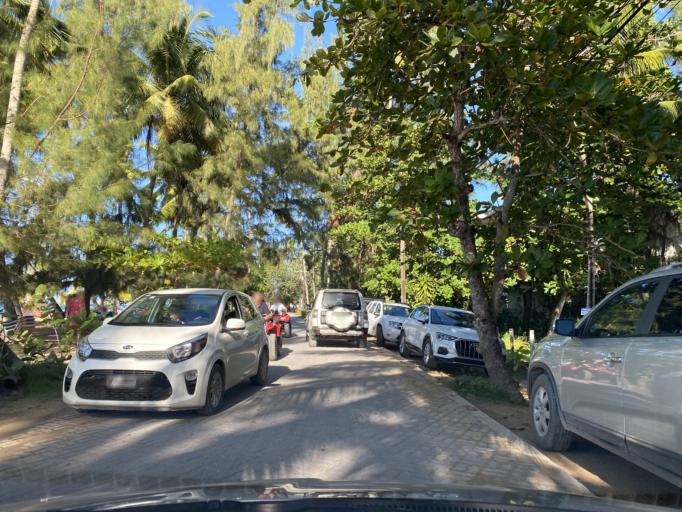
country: DO
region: Samana
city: Las Terrenas
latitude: 19.3245
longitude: -69.5524
